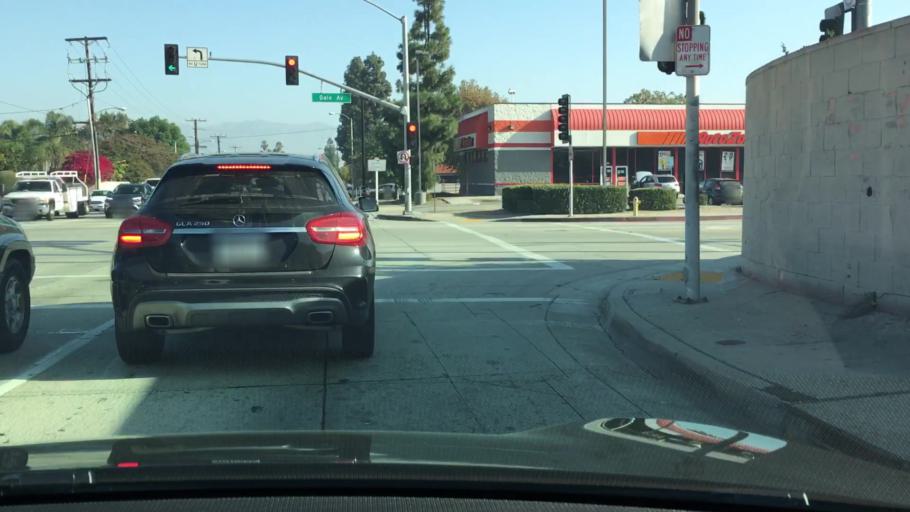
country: US
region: California
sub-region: Los Angeles County
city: Hacienda Heights
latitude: 34.0129
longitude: -117.9770
